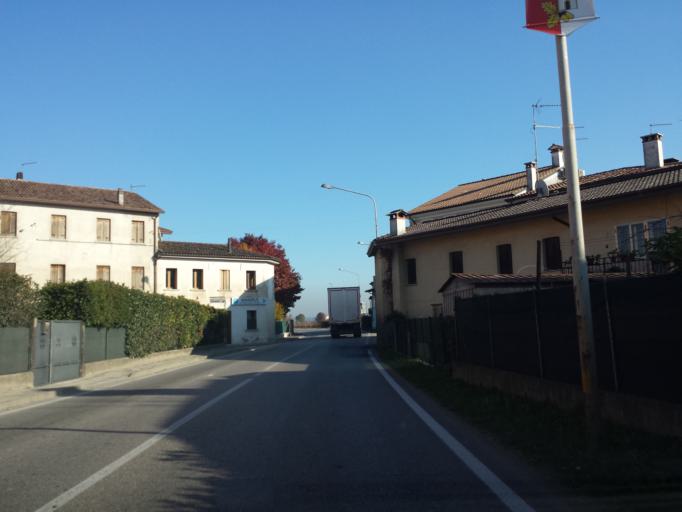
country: IT
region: Veneto
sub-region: Provincia di Treviso
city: Vidor
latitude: 45.8581
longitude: 12.0598
